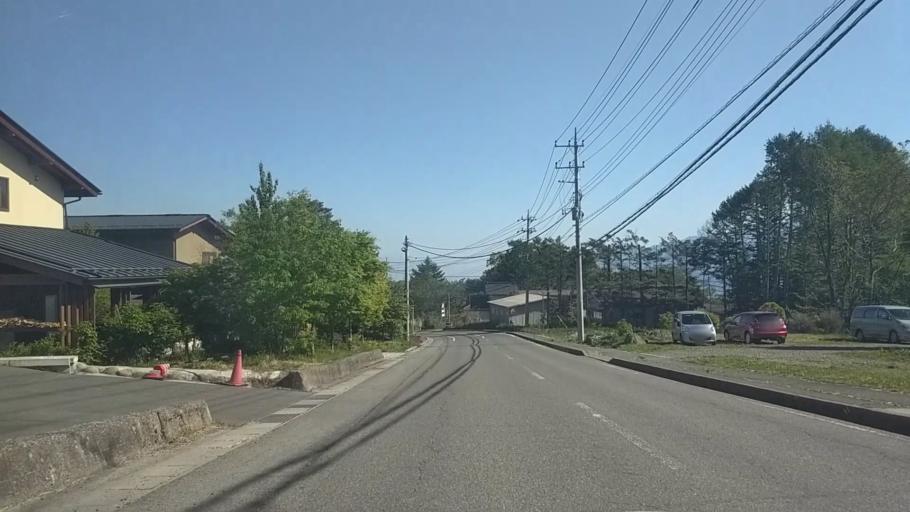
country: JP
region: Yamanashi
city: Nirasaki
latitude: 35.8993
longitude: 138.4100
